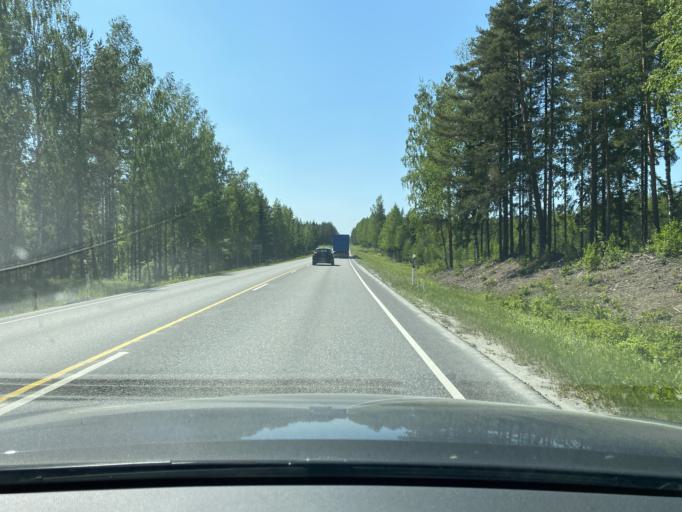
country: FI
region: Pirkanmaa
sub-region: Lounais-Pirkanmaa
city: Mouhijaervi
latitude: 61.3876
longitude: 23.2065
